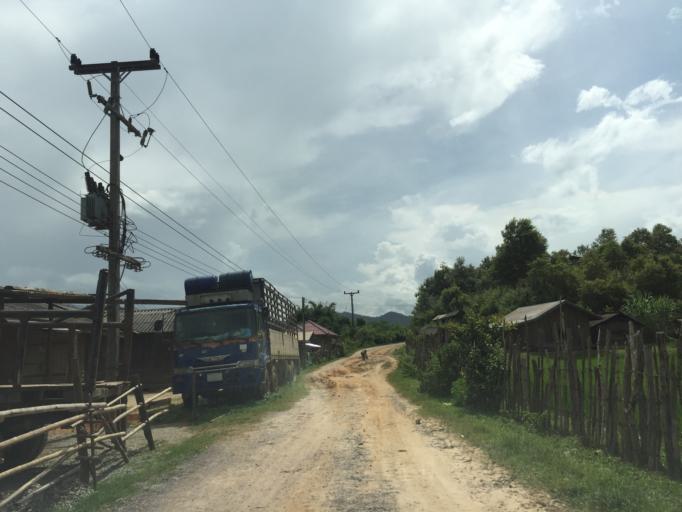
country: LA
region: Xiangkhoang
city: Muang Phonsavan
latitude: 19.3410
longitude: 103.5398
